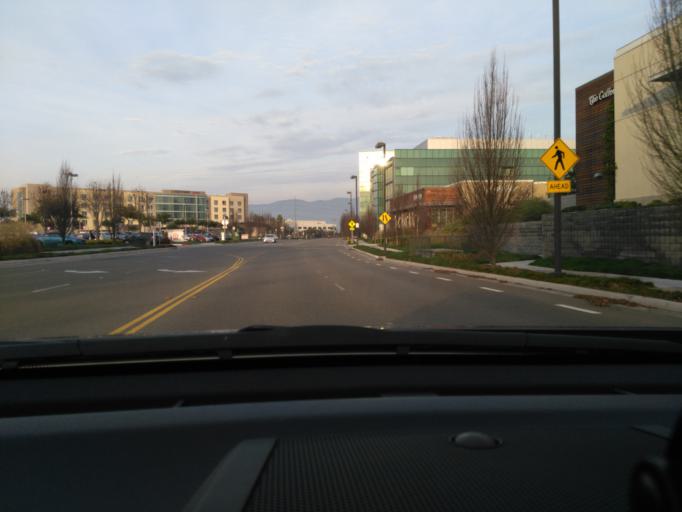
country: US
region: California
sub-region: Santa Clara County
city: Milpitas
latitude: 37.4169
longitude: -121.9554
